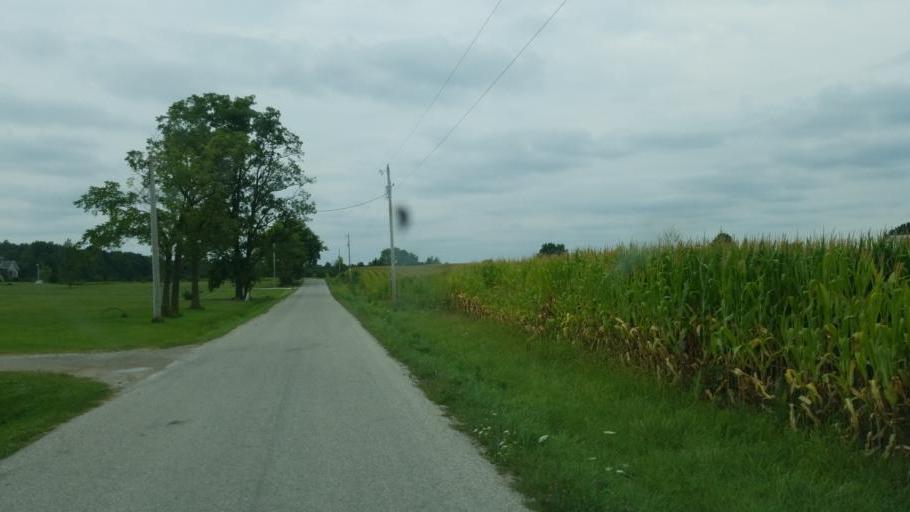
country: US
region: Ohio
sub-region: Morrow County
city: Mount Gilead
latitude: 40.5297
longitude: -82.8115
